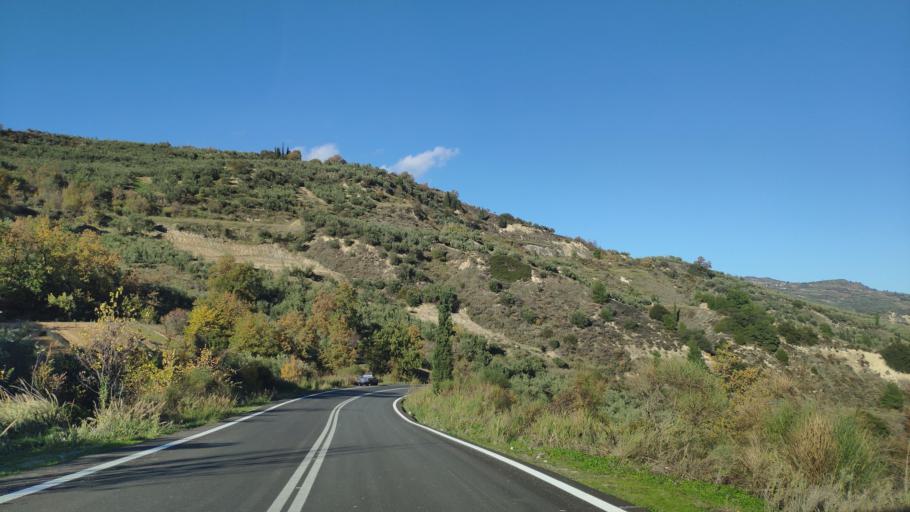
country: GR
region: Peloponnese
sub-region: Nomos Korinthias
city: Xylokastro
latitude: 38.0008
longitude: 22.5057
